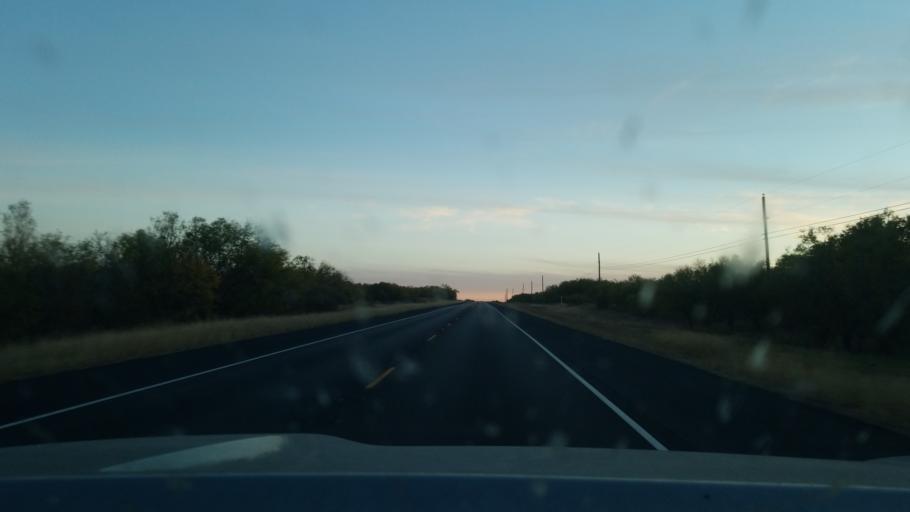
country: US
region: Texas
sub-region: Stephens County
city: Breckenridge
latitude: 32.6453
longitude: -98.9029
